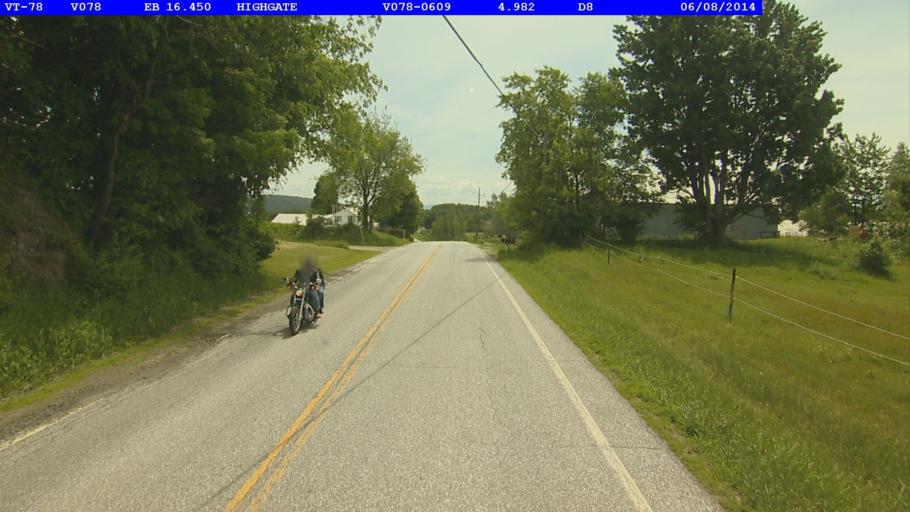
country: US
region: Vermont
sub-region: Franklin County
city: Swanton
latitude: 44.9436
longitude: -73.0107
